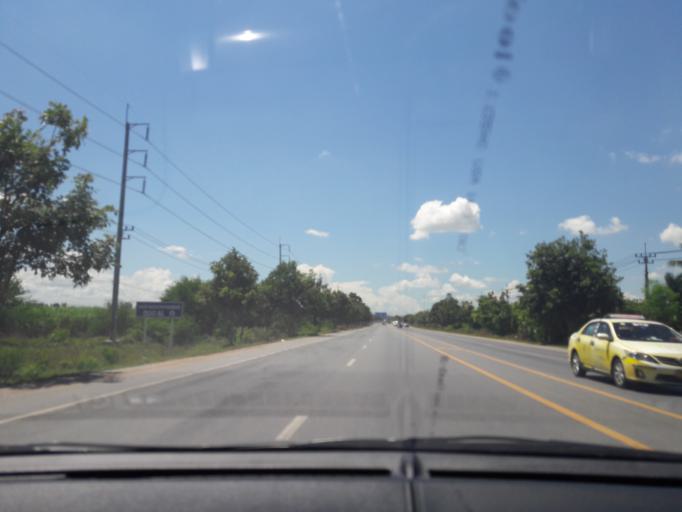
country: TH
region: Kanchanaburi
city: Tha Maka
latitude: 14.0354
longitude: 99.8117
